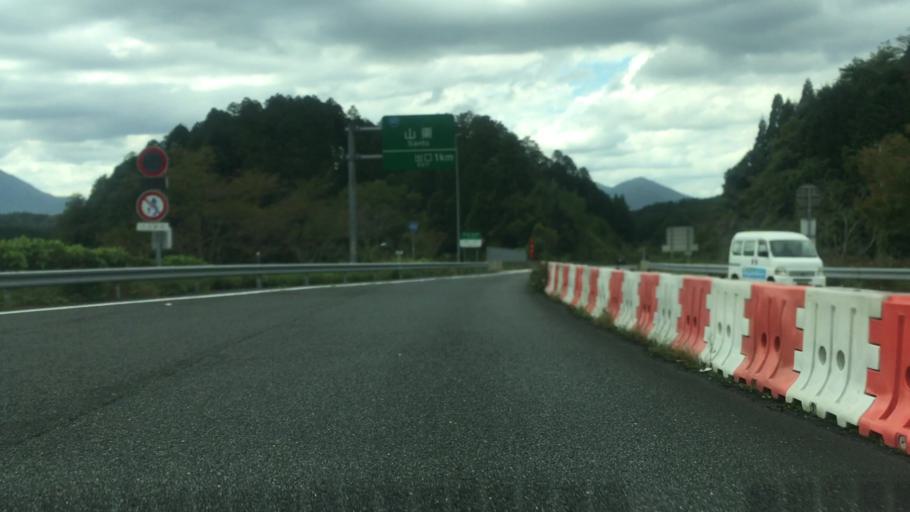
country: JP
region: Kyoto
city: Fukuchiyama
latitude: 35.3031
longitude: 134.9216
